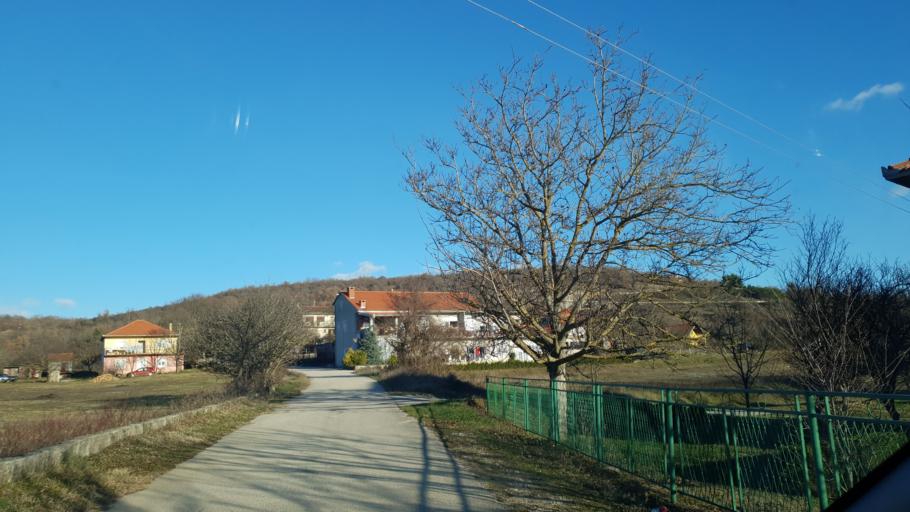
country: HR
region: Splitsko-Dalmatinska
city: Gala
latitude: 43.7375
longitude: 16.6829
